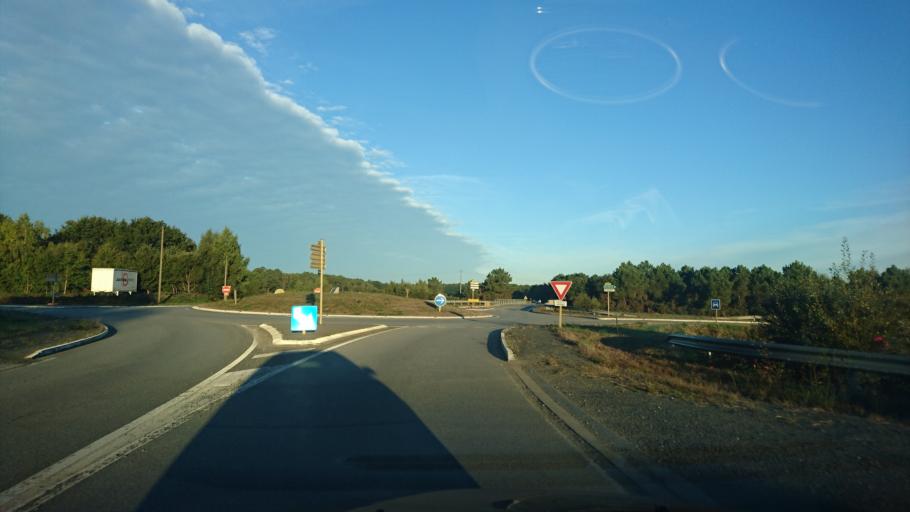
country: FR
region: Brittany
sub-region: Departement d'Ille-et-Vilaine
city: Sainte-Marie
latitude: 47.6986
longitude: -2.0200
